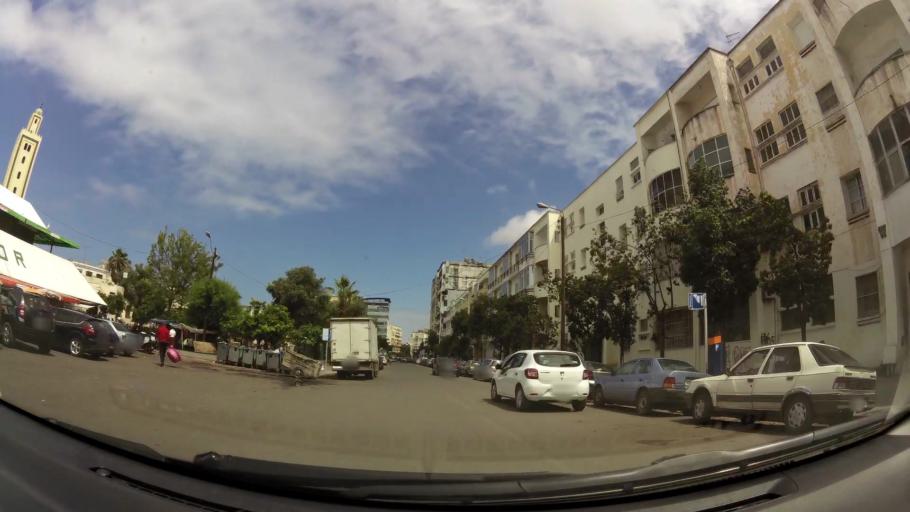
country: MA
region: Grand Casablanca
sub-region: Casablanca
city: Casablanca
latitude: 33.5933
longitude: -7.6399
